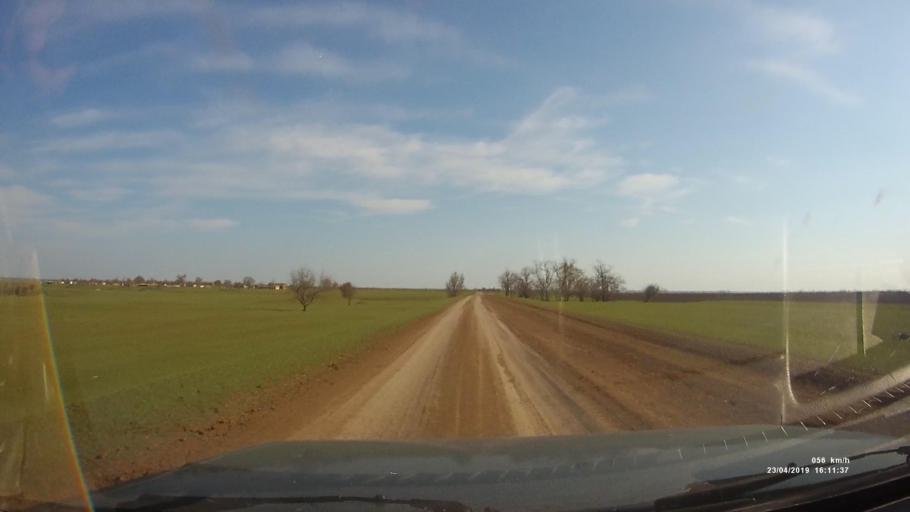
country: RU
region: Rostov
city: Remontnoye
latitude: 46.4735
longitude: 43.1226
